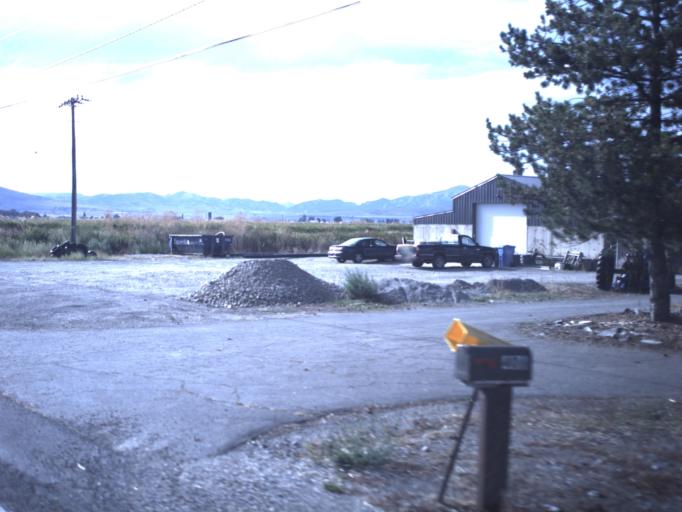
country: US
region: Utah
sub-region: Cache County
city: Lewiston
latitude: 41.9758
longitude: -111.8689
